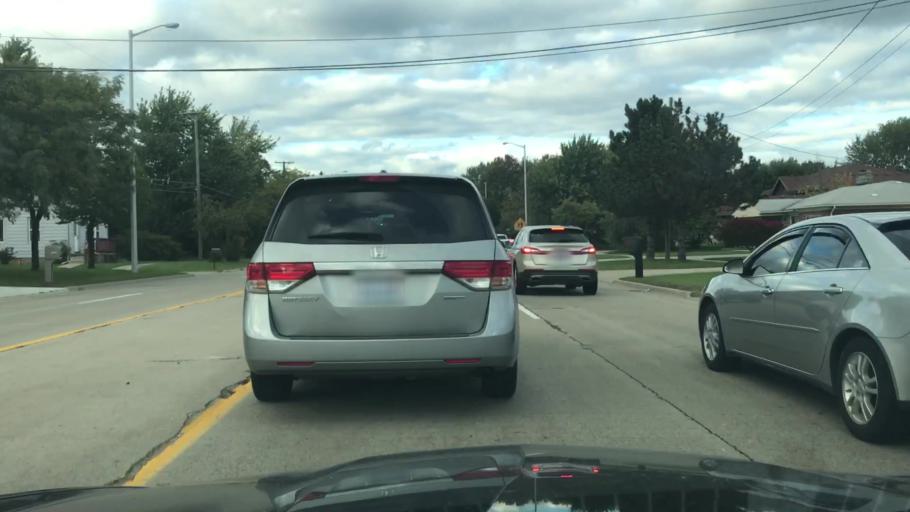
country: US
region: Michigan
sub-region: Macomb County
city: Sterling Heights
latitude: 42.5844
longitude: -83.0704
